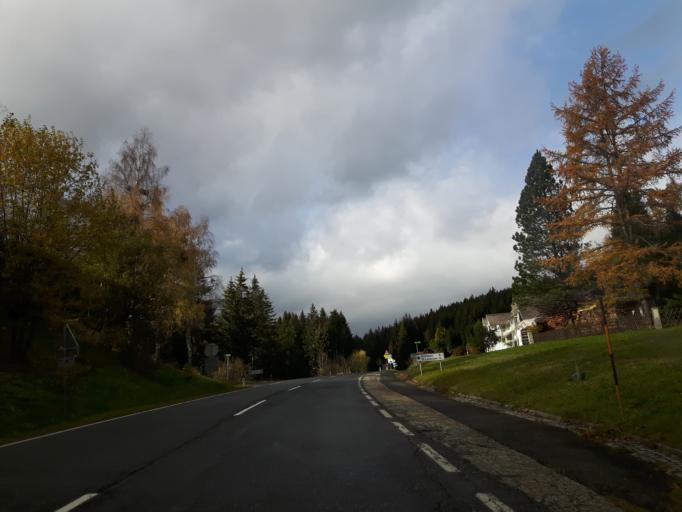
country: AT
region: Styria
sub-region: Politischer Bezirk Deutschlandsberg
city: Sankt Oswald ob Eibiswald
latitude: 46.6994
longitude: 15.1144
